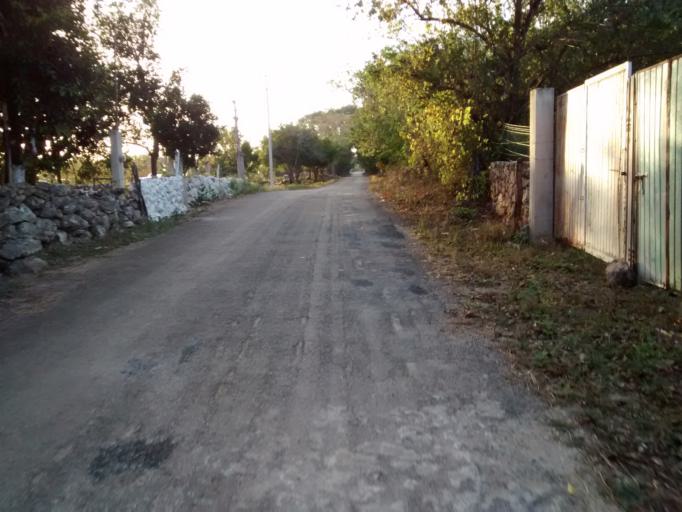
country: MX
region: Yucatan
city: Valladolid
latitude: 20.6809
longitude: -88.1616
